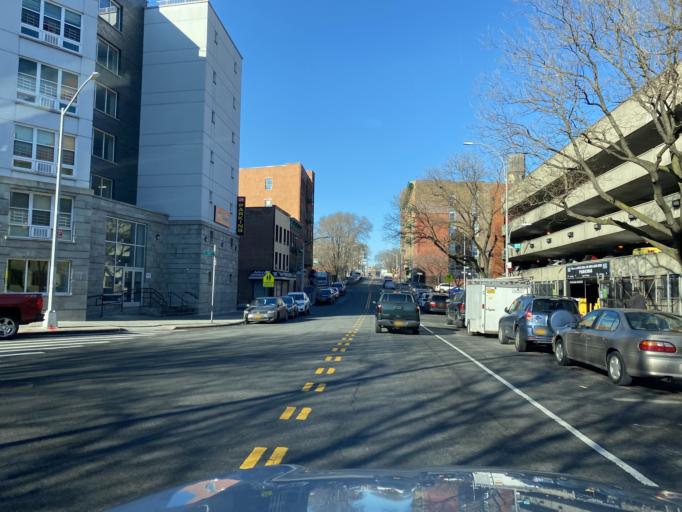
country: US
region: New York
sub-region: New York County
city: Inwood
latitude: 40.8156
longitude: -73.9245
